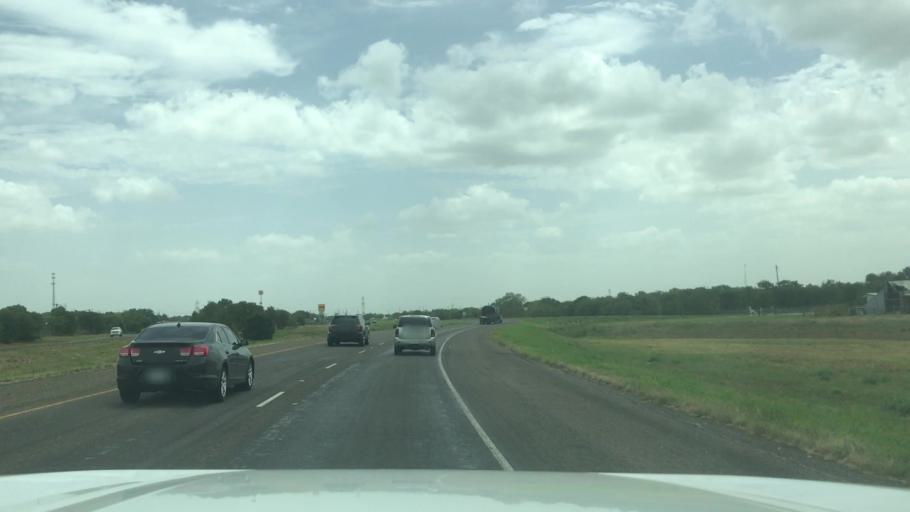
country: US
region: Texas
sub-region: McLennan County
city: Riesel
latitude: 31.4815
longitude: -96.9263
